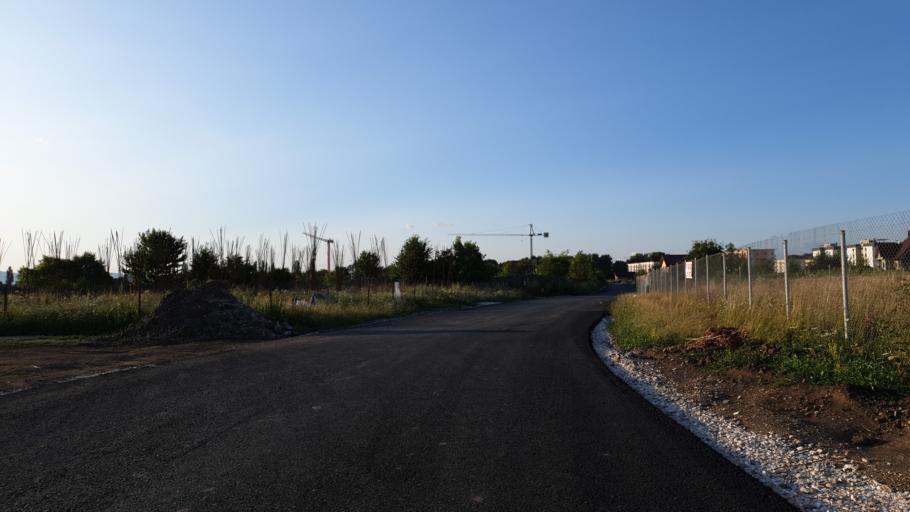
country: RO
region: Brasov
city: Brasov
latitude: 45.6767
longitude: 25.6047
